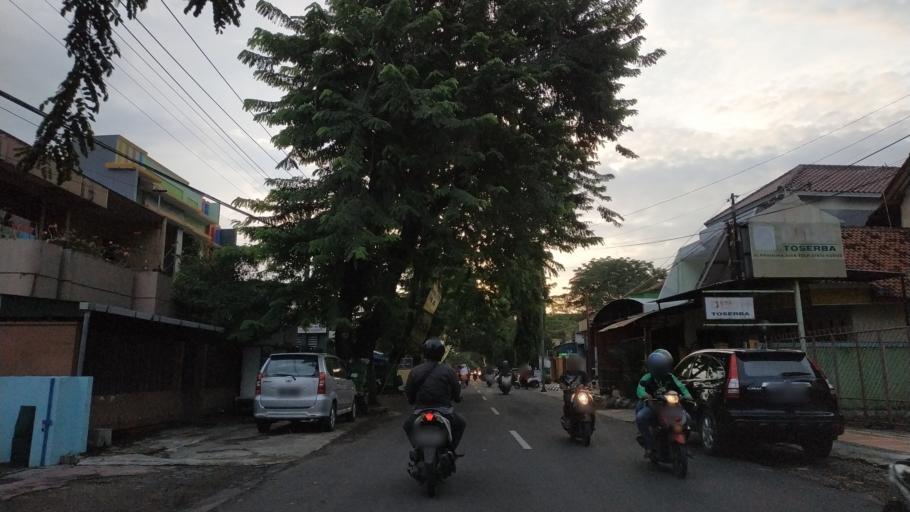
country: ID
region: Central Java
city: Kudus
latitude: -6.8121
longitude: 110.8527
